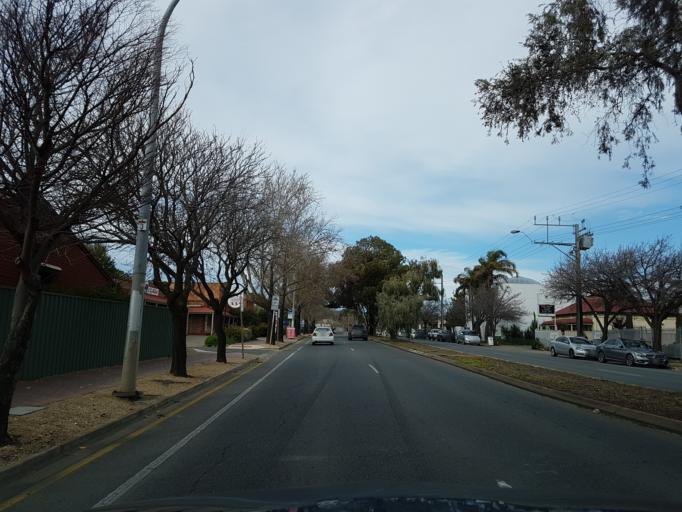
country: AU
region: South Australia
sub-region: Norwood Payneham St Peters
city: Trinity Gardens
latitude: -34.9134
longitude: 138.6305
